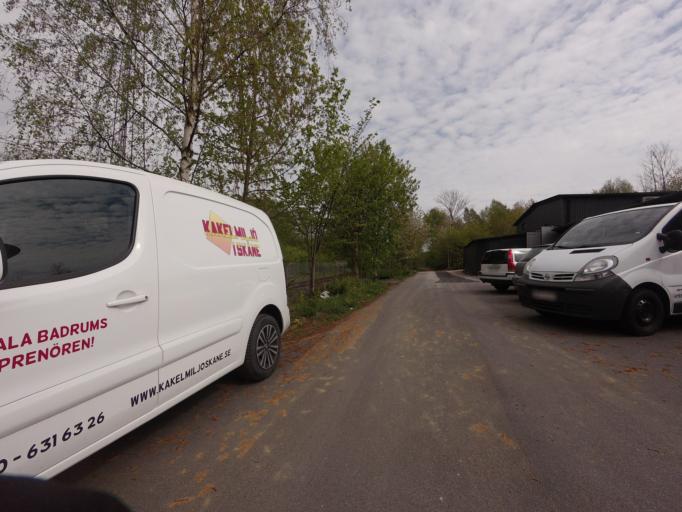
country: SE
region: Skane
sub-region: Malmo
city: Oxie
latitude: 55.5440
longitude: 13.0857
